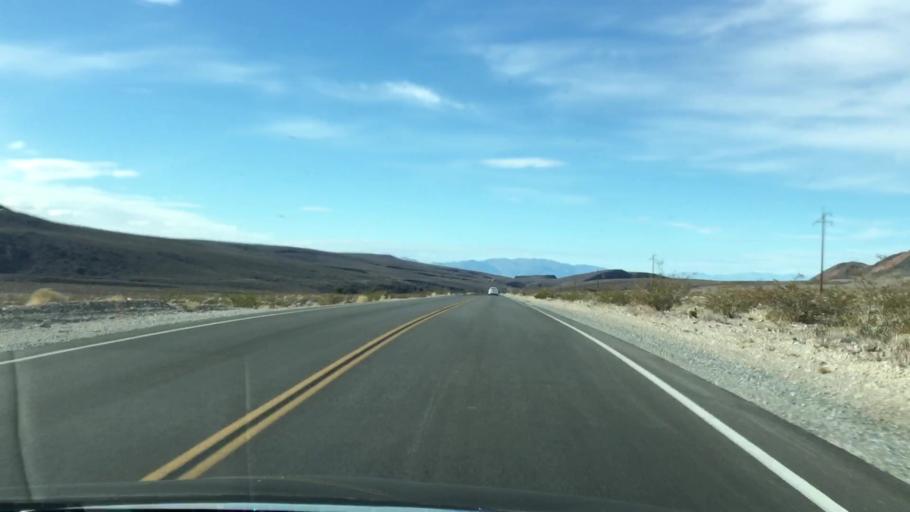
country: US
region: Nevada
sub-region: Nye County
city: Beatty
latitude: 36.3465
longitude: -116.6191
